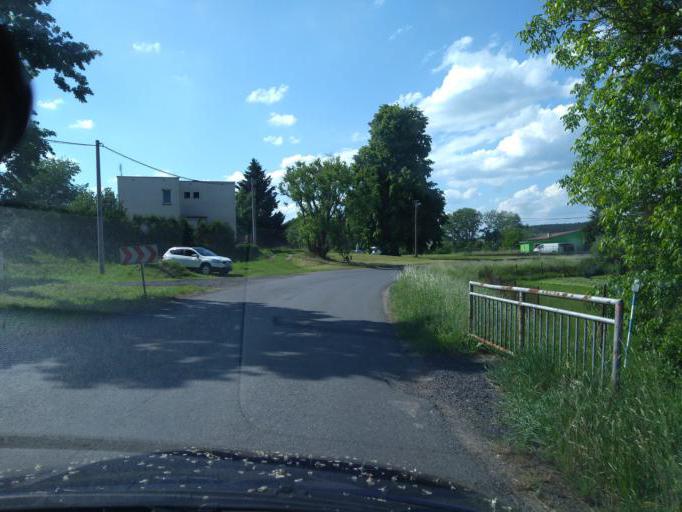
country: CZ
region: Plzensky
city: Chotesov
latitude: 49.6152
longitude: 13.2369
